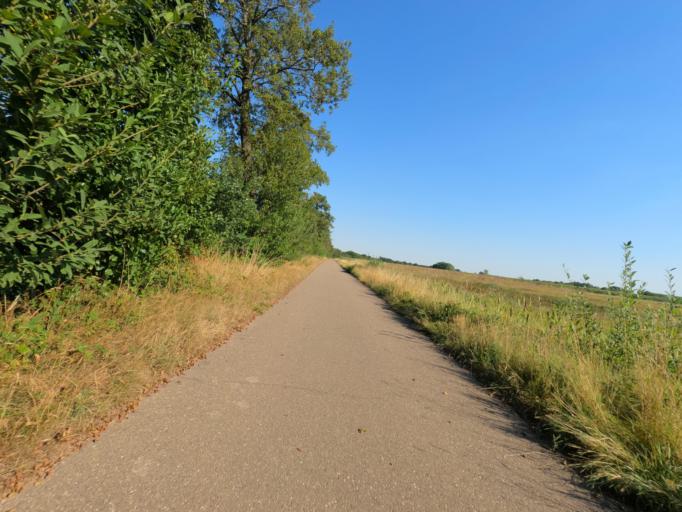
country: NL
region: Limburg
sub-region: Gemeente Roerdalen
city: Vlodrop
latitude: 51.1482
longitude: 6.0870
